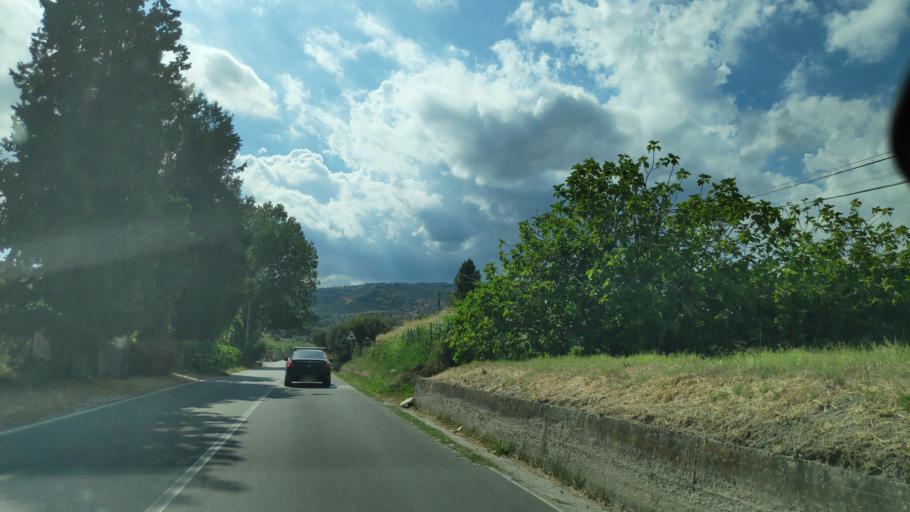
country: IT
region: Calabria
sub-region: Provincia di Catanzaro
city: Santa Caterina dello Ionio Marina
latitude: 38.5272
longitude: 16.5612
